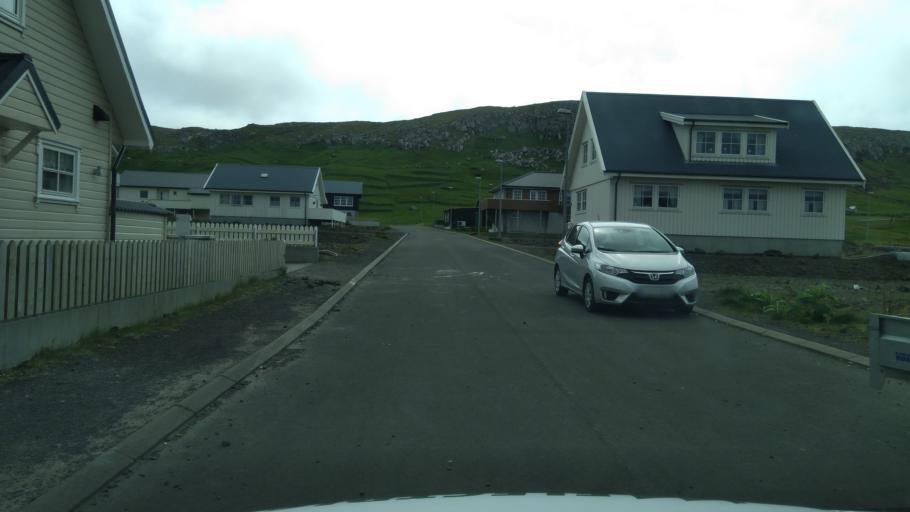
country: FO
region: Sandoy
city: Sandur
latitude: 61.9050
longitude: -6.8913
